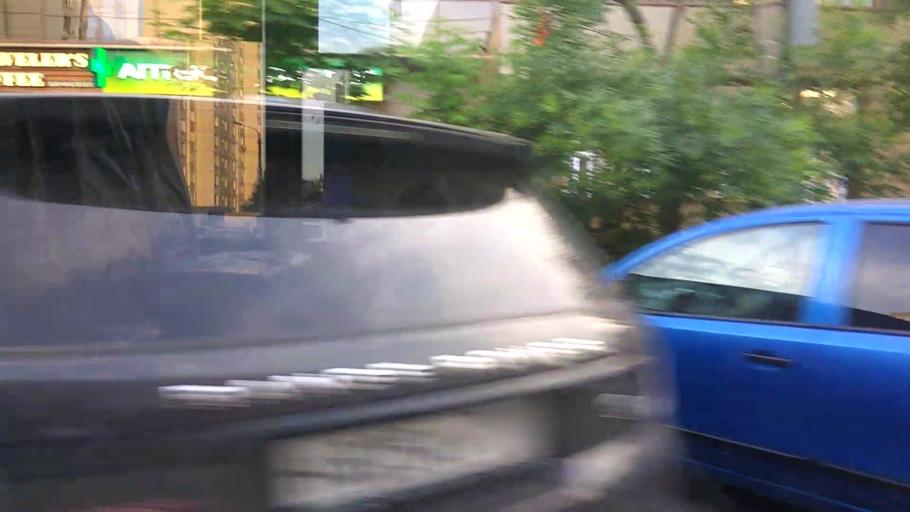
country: RU
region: Moskovskaya
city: Yubileyny
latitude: 55.9199
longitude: 37.8682
